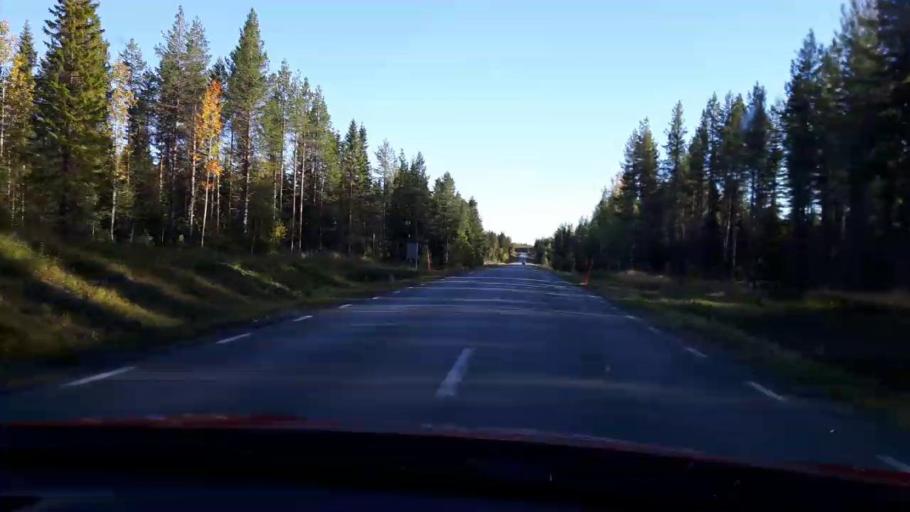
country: SE
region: Jaemtland
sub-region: OEstersunds Kommun
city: Lit
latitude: 63.7901
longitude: 14.7035
